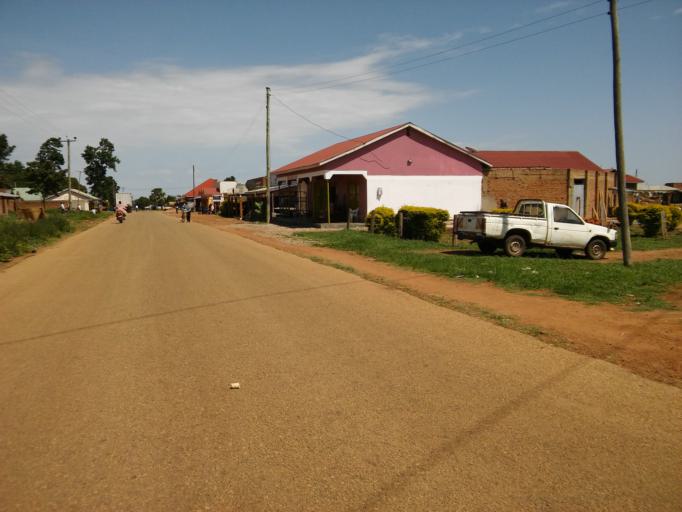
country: UG
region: Eastern Region
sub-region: Kumi District
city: Kumi
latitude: 1.4869
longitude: 33.9295
